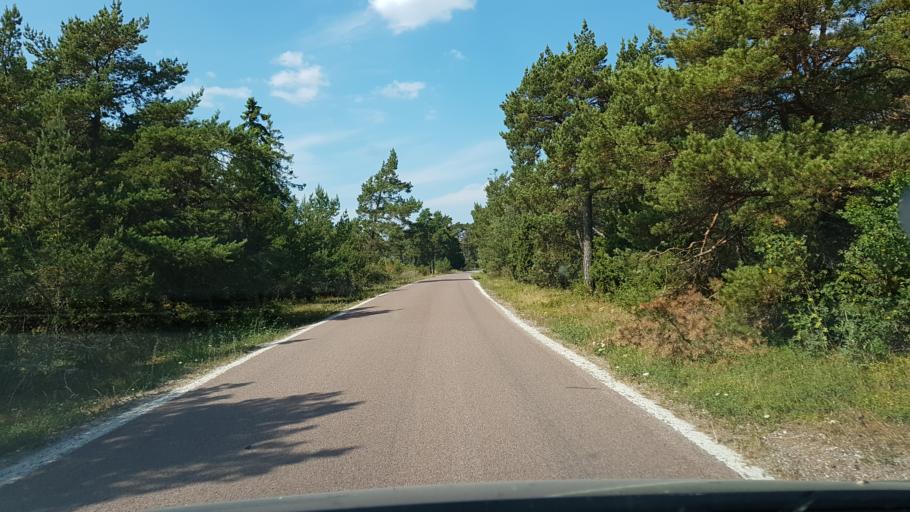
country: SE
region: Gotland
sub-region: Gotland
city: Visby
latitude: 57.6713
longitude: 18.3634
